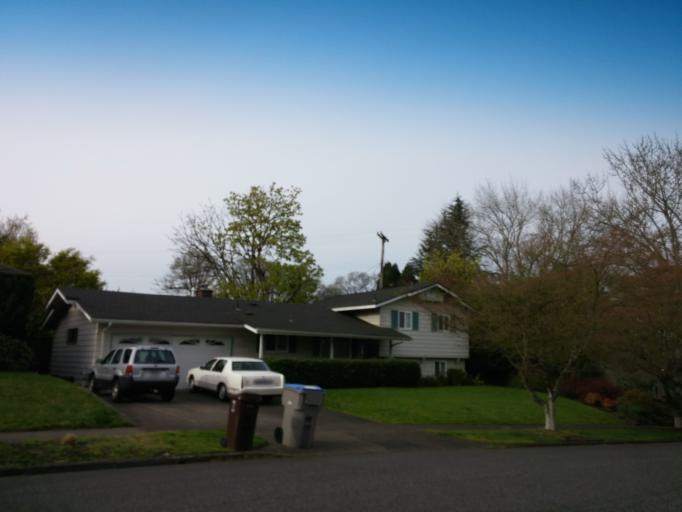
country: US
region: Oregon
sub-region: Washington County
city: Cedar Hills
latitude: 45.5092
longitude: -122.8085
